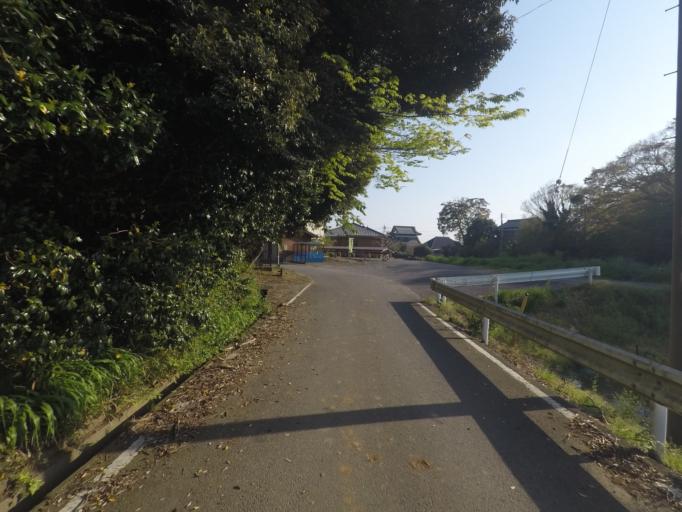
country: JP
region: Ibaraki
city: Inashiki
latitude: 36.0663
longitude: 140.3586
